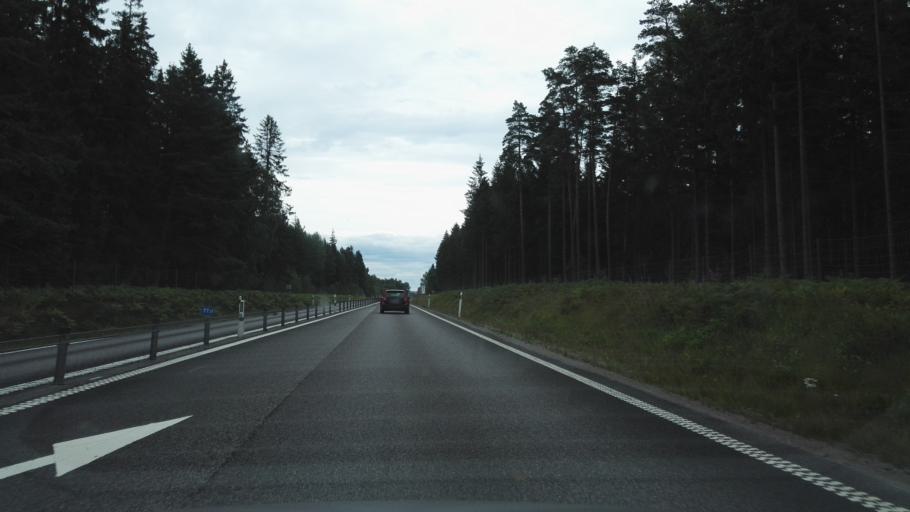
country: SE
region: Kronoberg
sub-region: Vaxjo Kommun
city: Rottne
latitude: 56.9570
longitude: 14.9413
